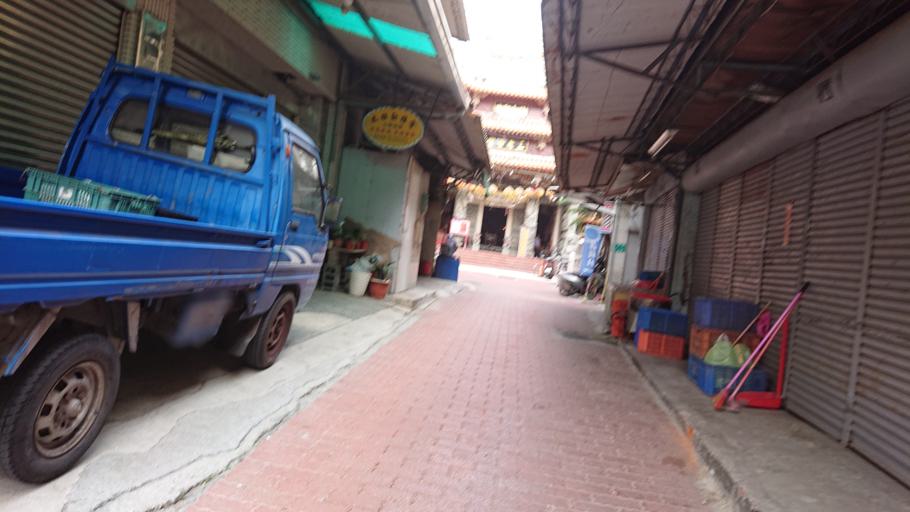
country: TW
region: Taiwan
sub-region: Tainan
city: Tainan
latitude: 22.9998
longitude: 120.2048
